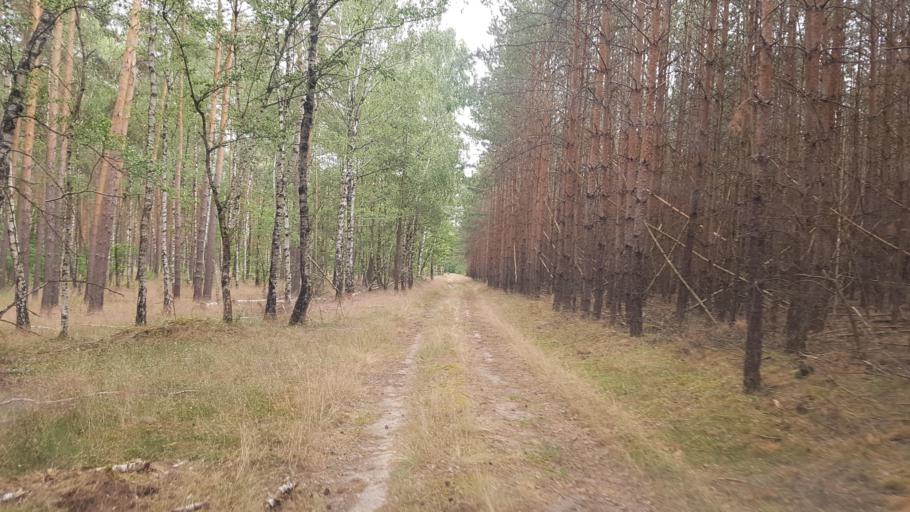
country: DE
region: Brandenburg
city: Treuenbrietzen
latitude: 52.0563
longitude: 12.8159
